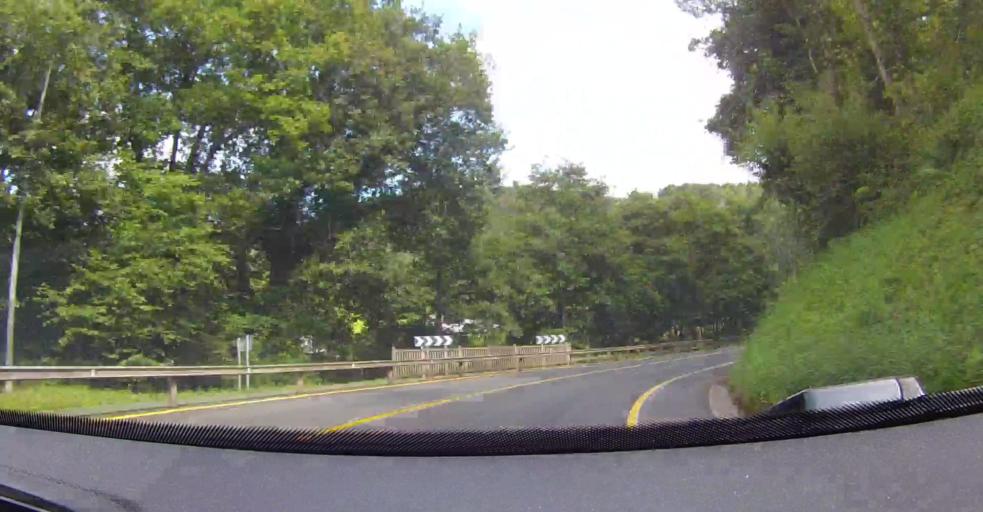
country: ES
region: Basque Country
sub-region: Bizkaia
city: Elantxobe
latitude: 43.3983
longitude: -2.6451
